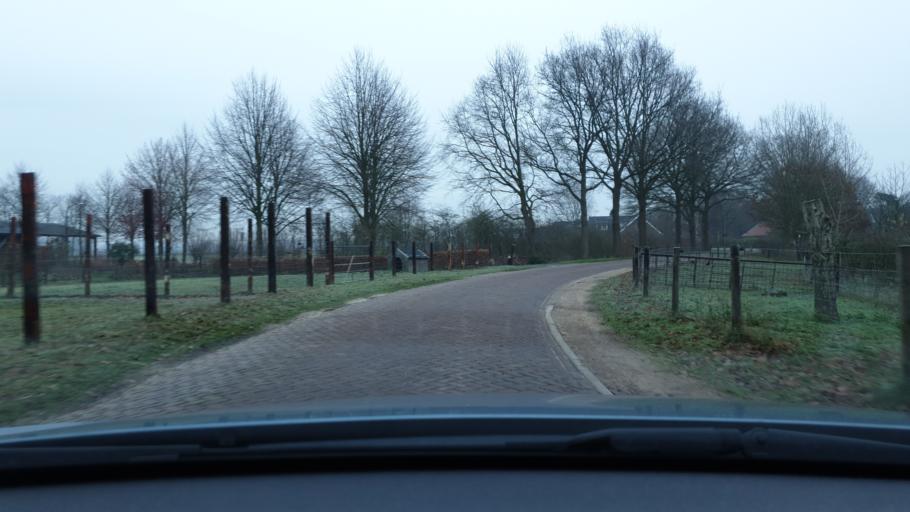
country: NL
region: Gelderland
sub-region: Gemeente Wijchen
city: Bergharen
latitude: 51.8645
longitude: 5.6590
